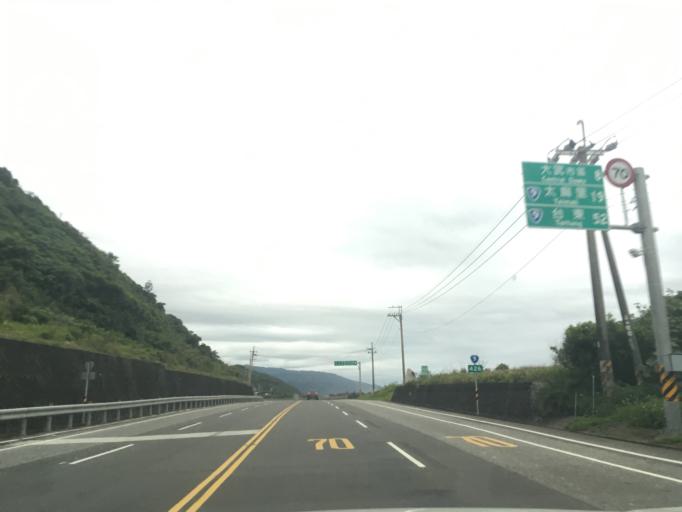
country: TW
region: Taiwan
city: Hengchun
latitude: 22.2961
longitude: 120.8886
